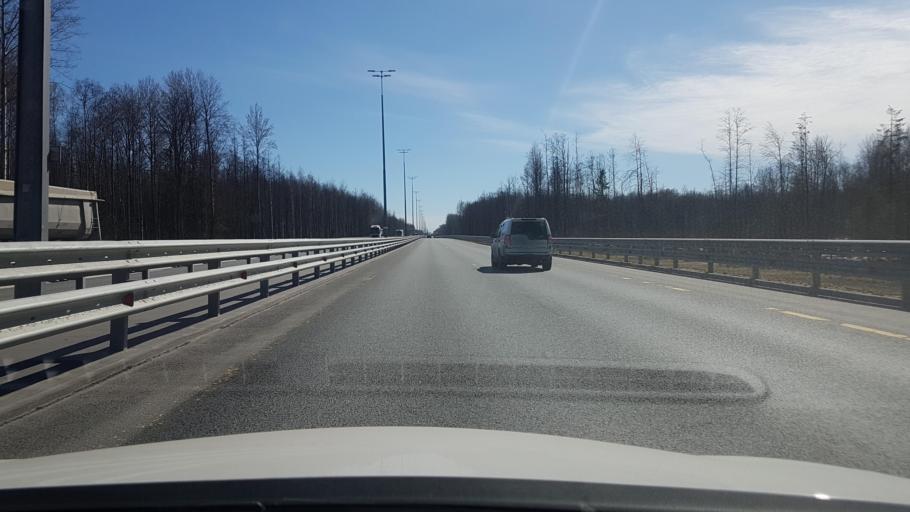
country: RU
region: Novgorod
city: Krechevitsy
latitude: 58.8474
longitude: 31.4218
